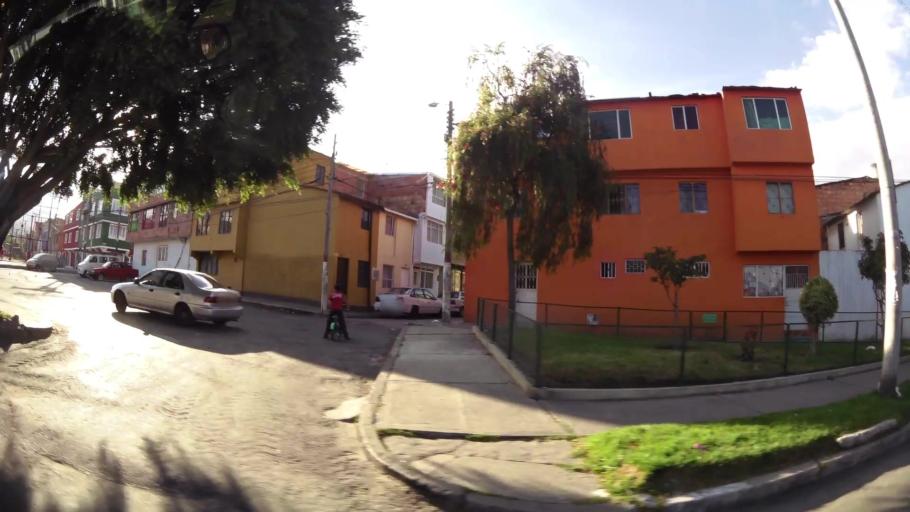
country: CO
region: Cundinamarca
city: Soacha
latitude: 4.5784
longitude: -74.1513
